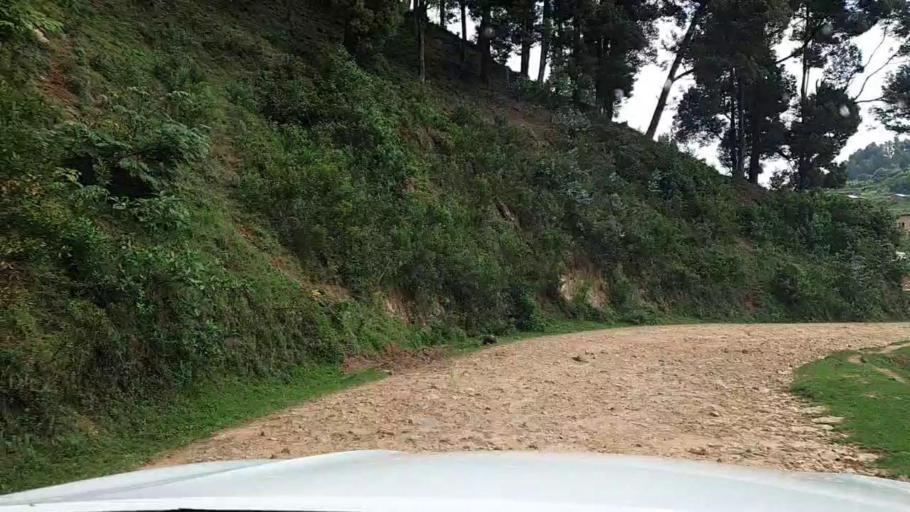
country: RW
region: Western Province
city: Kibuye
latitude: -2.2897
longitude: 29.3685
